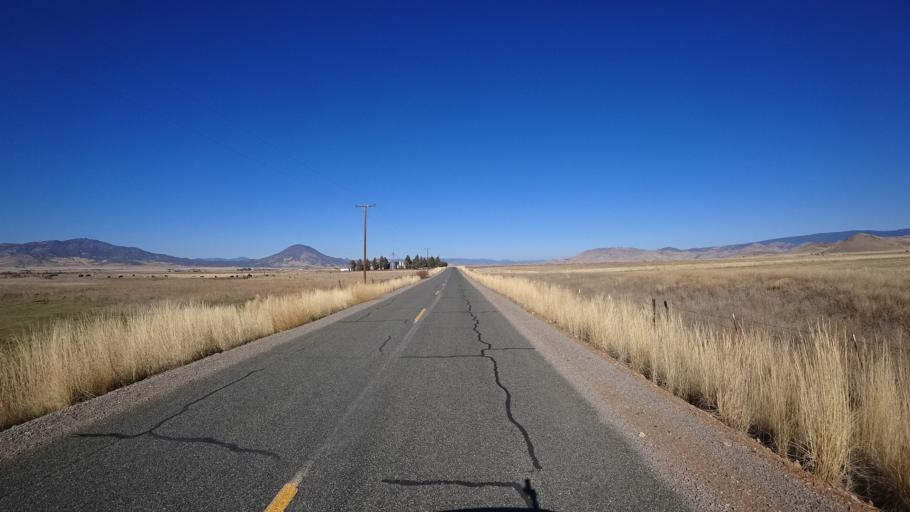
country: US
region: California
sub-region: Siskiyou County
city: Montague
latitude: 41.7601
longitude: -122.4571
